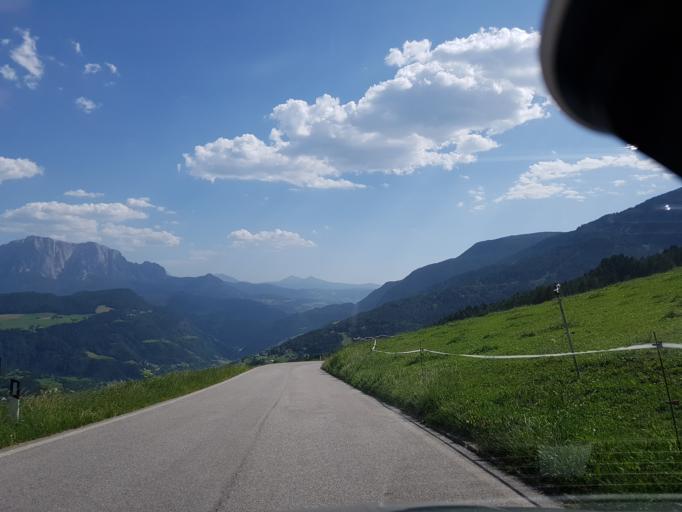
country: IT
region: Trentino-Alto Adige
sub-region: Bolzano
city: Villandro - Villanders
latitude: 46.6365
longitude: 11.5286
